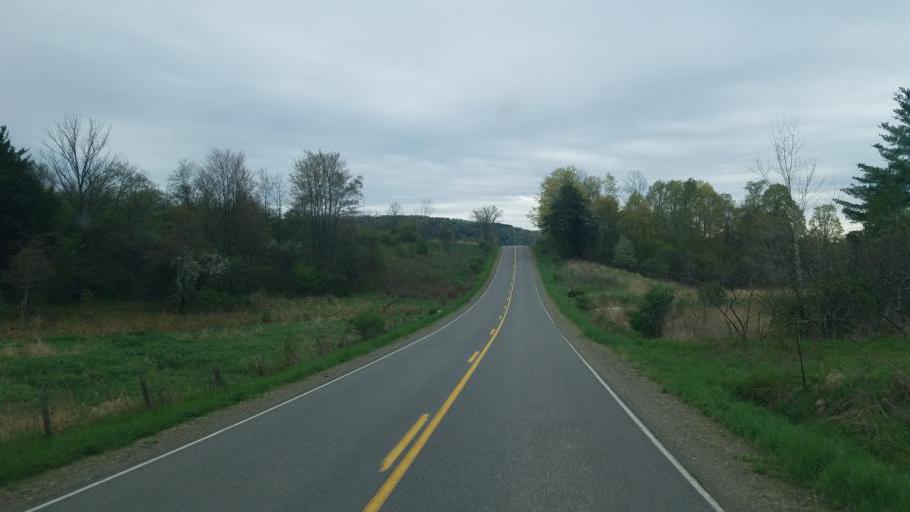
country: US
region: Pennsylvania
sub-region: Tioga County
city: Westfield
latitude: 42.0313
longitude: -77.4663
